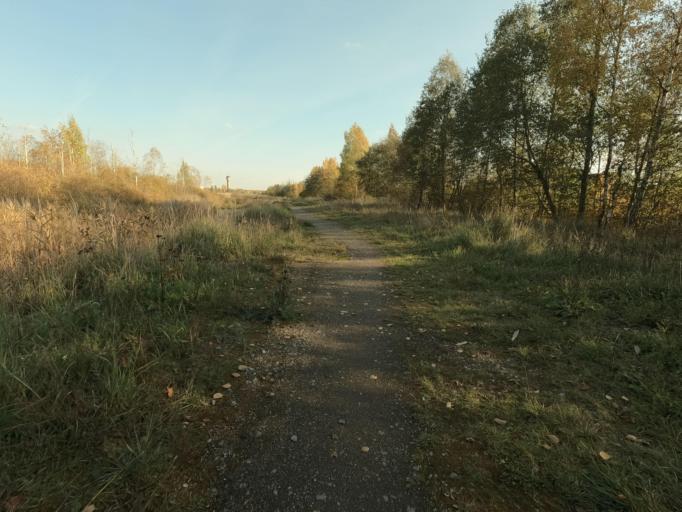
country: RU
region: Leningrad
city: Mga
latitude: 59.7489
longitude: 31.0680
